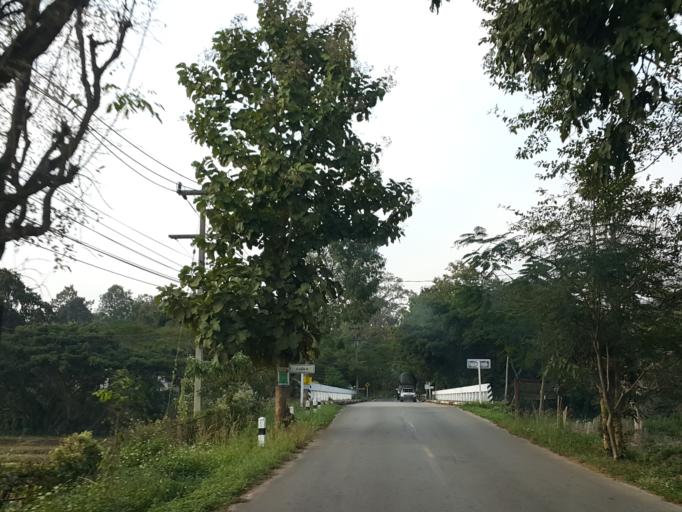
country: TH
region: Chiang Mai
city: Mae On
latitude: 18.8976
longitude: 99.2597
